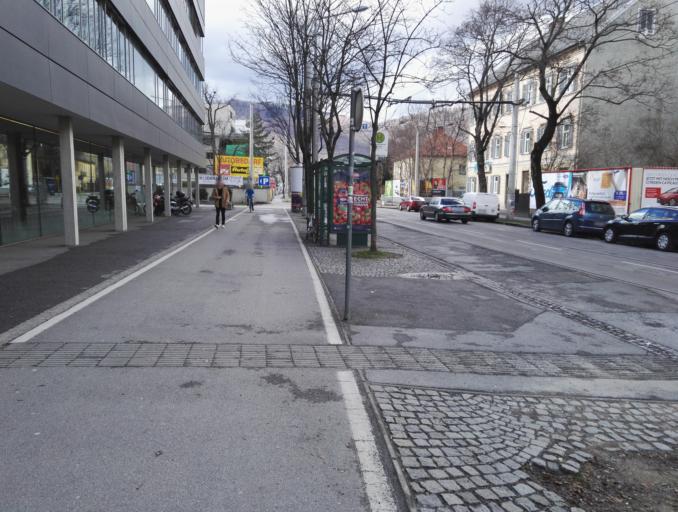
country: AT
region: Styria
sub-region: Graz Stadt
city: Wetzelsdorf
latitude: 47.0701
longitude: 15.4064
